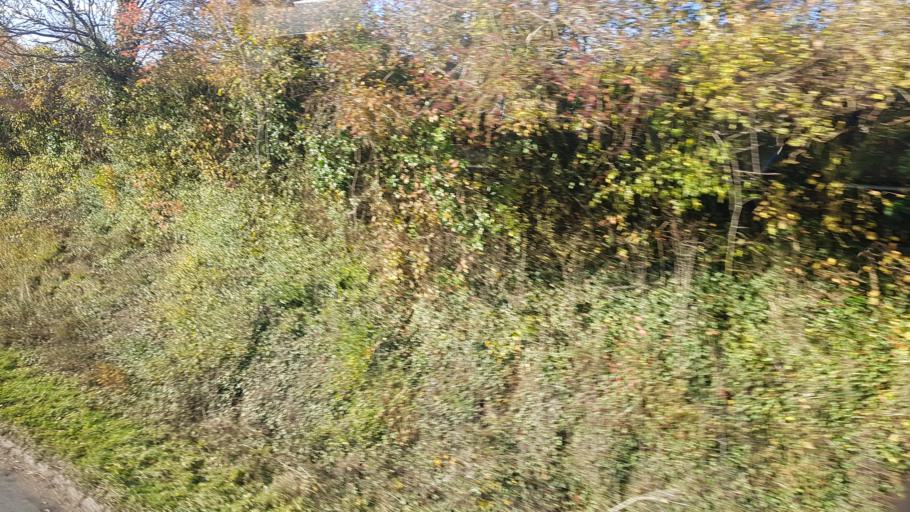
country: GB
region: England
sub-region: Isle of Wight
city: Newport
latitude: 50.6655
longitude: -1.3446
